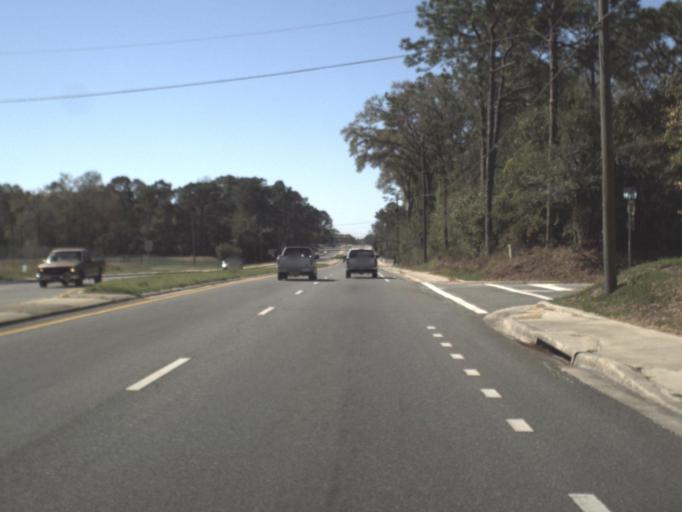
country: US
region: Florida
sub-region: Leon County
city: Tallahassee
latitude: 30.3864
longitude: -84.2874
